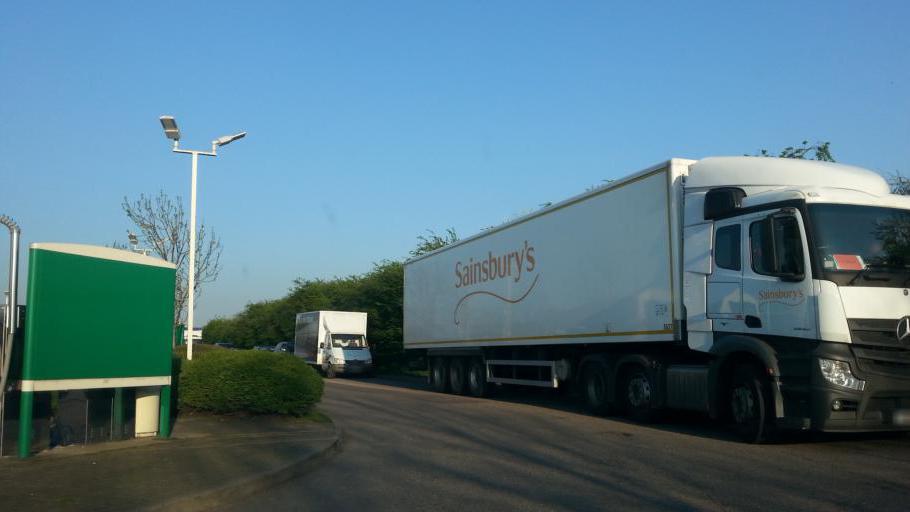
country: GB
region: England
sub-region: Northamptonshire
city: Raunds
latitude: 52.3533
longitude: -0.5466
